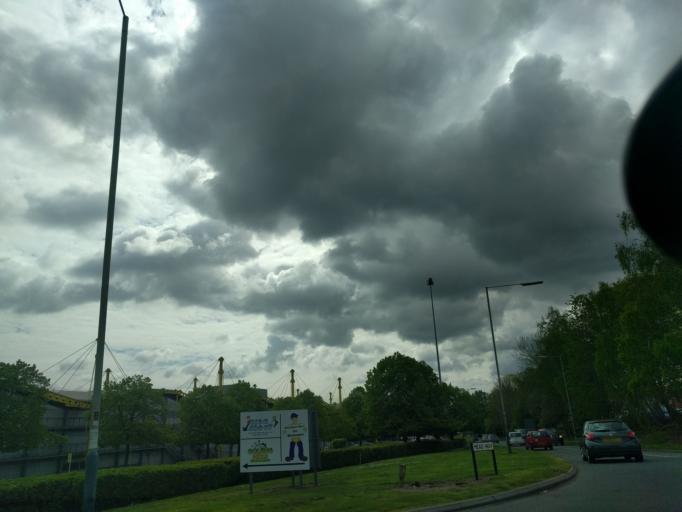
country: GB
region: England
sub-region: Wiltshire
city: Lydiard Tregoze
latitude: 51.5666
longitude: -1.8255
